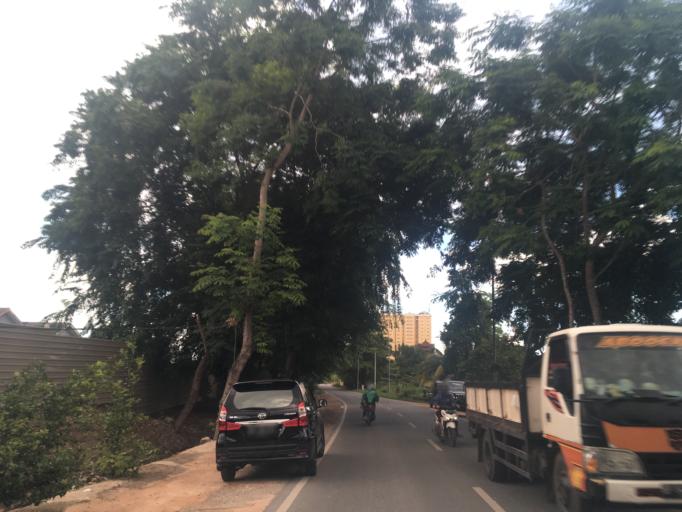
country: SG
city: Singapore
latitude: 1.1223
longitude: 104.0260
